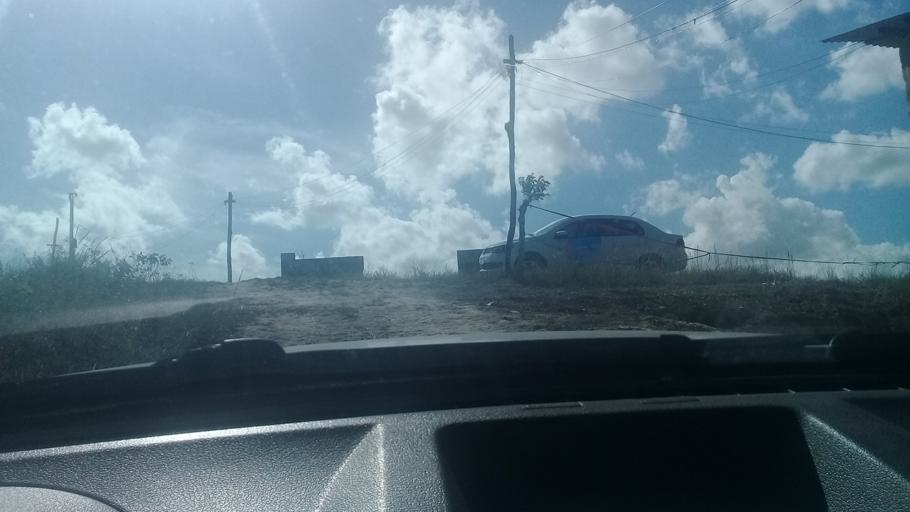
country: BR
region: Pernambuco
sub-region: Jaboatao Dos Guararapes
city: Jaboatao dos Guararapes
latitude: -8.0823
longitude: -35.0362
